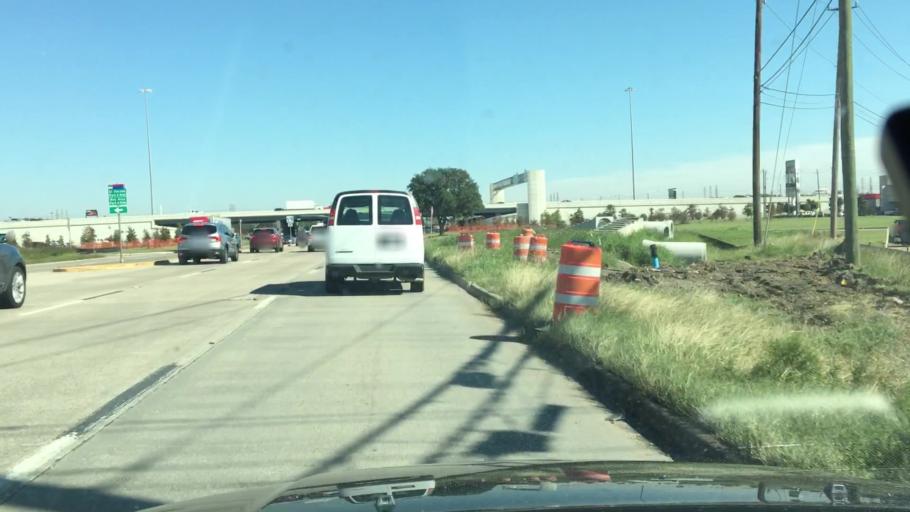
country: US
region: Texas
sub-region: Harris County
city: Webster
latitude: 29.5269
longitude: -95.1329
